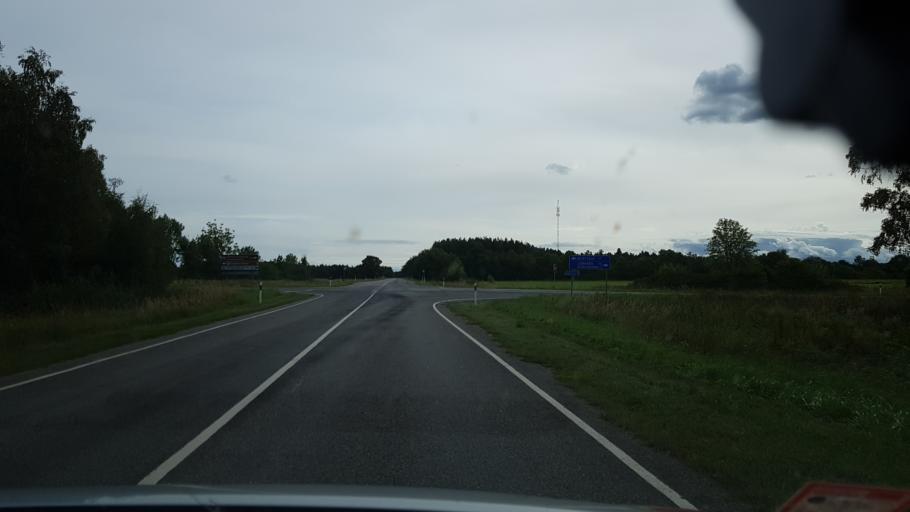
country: EE
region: Saare
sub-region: Kuressaare linn
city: Kuressaare
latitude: 58.3649
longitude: 22.0549
